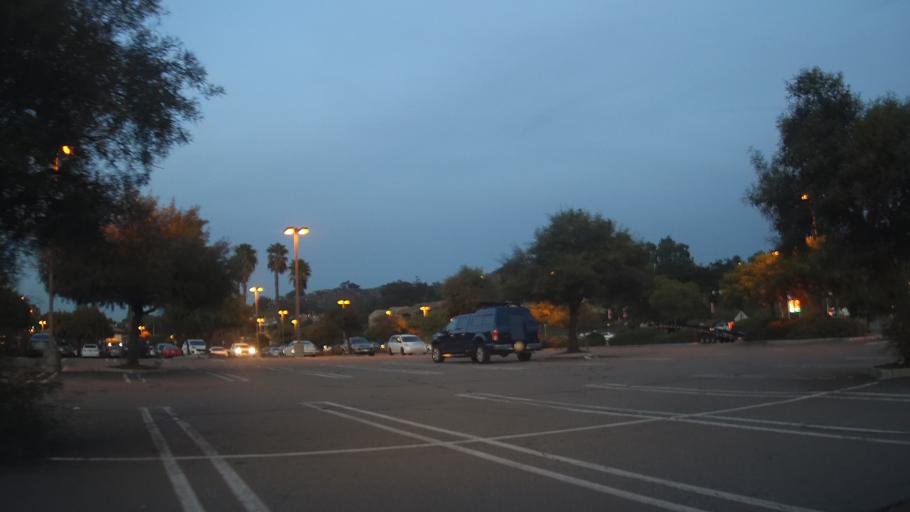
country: US
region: California
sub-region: San Diego County
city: Rancho San Diego
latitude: 32.7457
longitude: -116.9290
